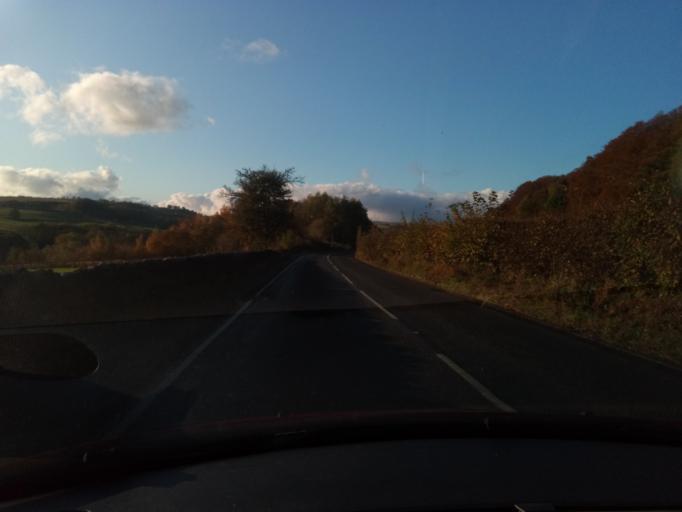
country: GB
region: England
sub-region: County Durham
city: Stanhope
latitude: 54.7339
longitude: -1.9808
